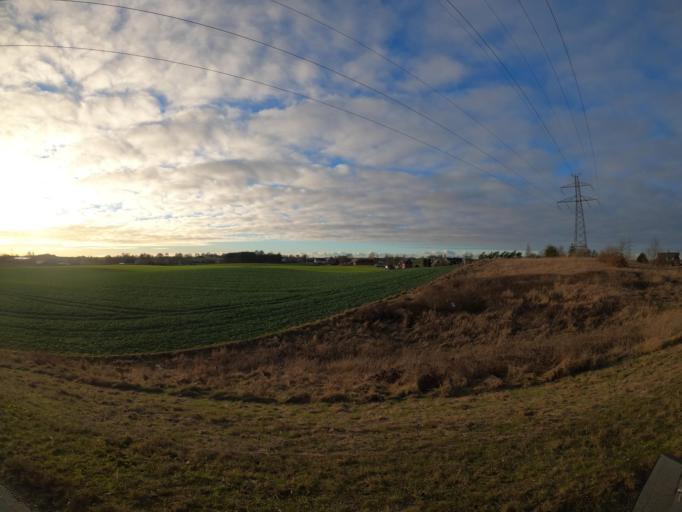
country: SE
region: Skane
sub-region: Svedala Kommun
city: Svedala
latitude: 55.5075
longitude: 13.2154
